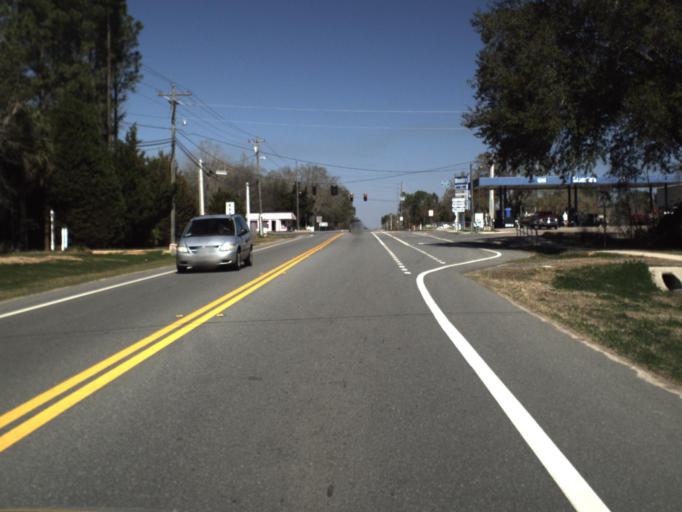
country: US
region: Florida
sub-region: Jackson County
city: Sneads
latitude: 30.7177
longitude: -85.0202
